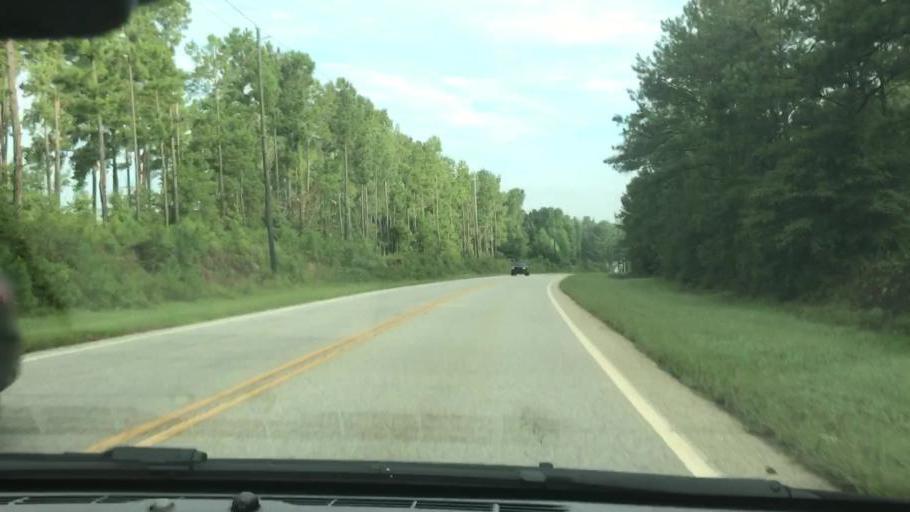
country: US
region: Georgia
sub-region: Clay County
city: Fort Gaines
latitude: 31.7426
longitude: -85.0531
